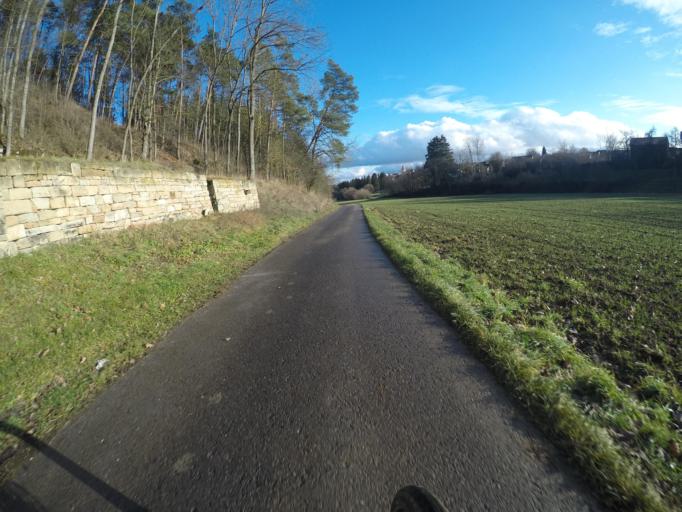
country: DE
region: Baden-Wuerttemberg
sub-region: Regierungsbezirk Stuttgart
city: Herrenberg
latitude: 48.5551
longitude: 8.8684
